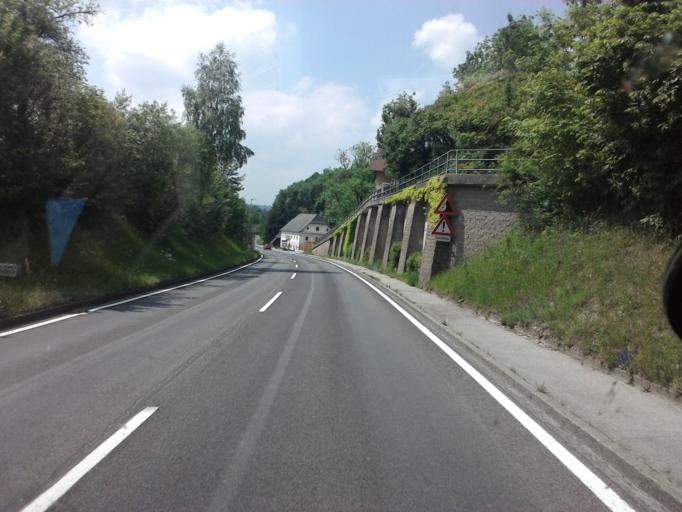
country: AT
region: Upper Austria
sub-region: Politischer Bezirk Steyr-Land
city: Garsten
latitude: 48.0456
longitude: 14.3772
